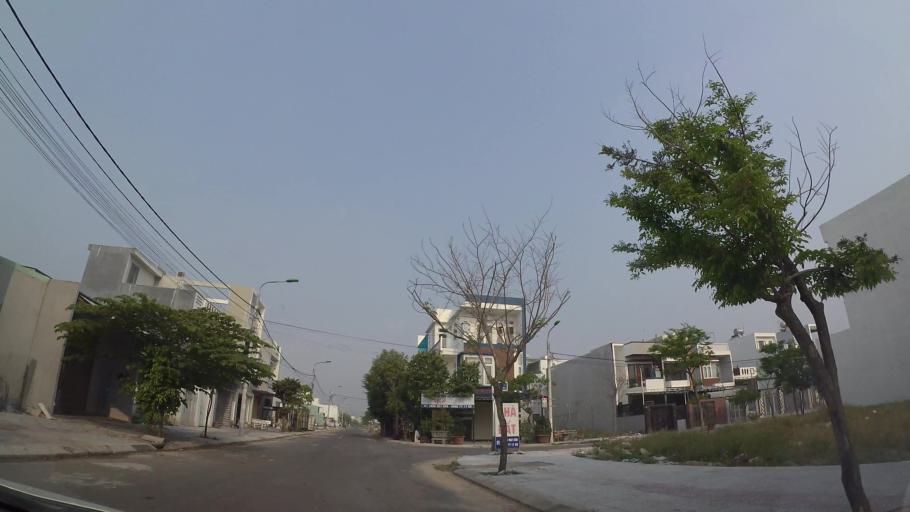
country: VN
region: Da Nang
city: Cam Le
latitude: 16.0065
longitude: 108.2276
